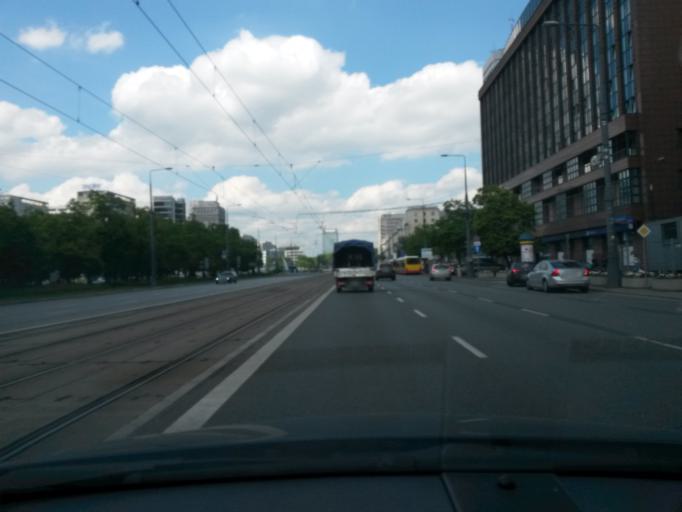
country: PL
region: Masovian Voivodeship
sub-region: Warszawa
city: Warsaw
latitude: 52.2334
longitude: 21.0097
